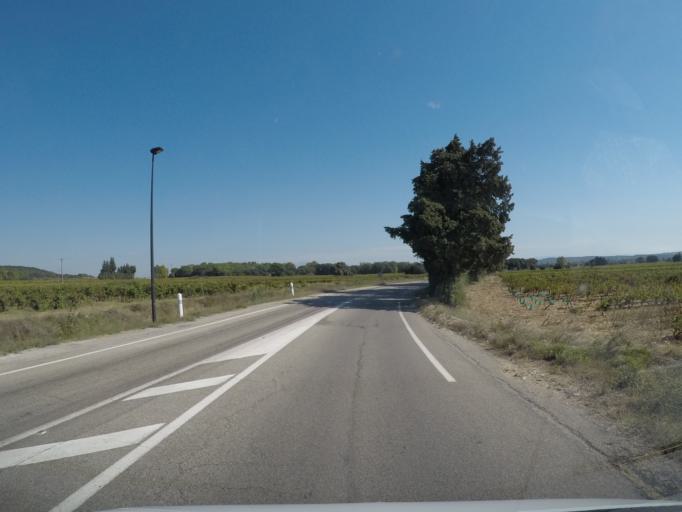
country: FR
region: Languedoc-Roussillon
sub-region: Departement du Gard
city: Tavel
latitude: 44.0098
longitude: 4.7229
